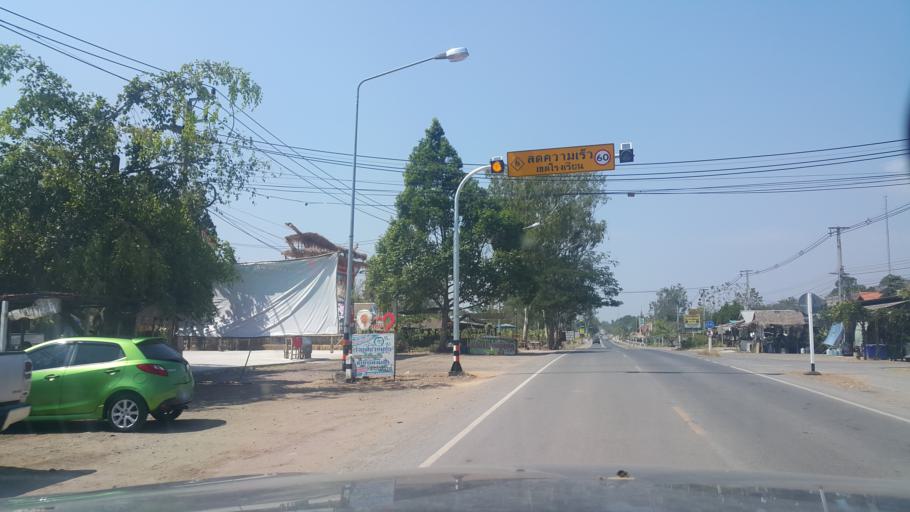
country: TH
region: Nakhon Ratchasima
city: Wang Nam Khiao
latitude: 14.3597
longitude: 101.9195
